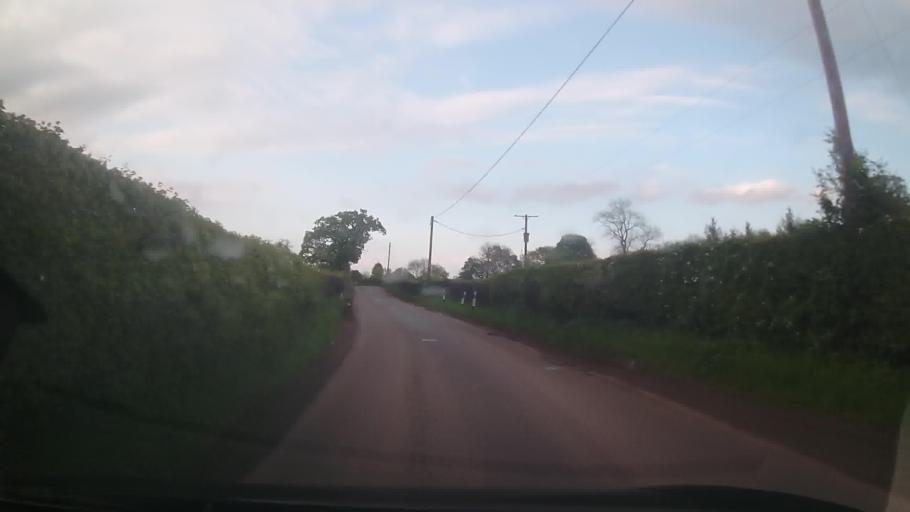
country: GB
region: England
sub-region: Shropshire
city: Ellesmere
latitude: 52.9404
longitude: -2.8736
